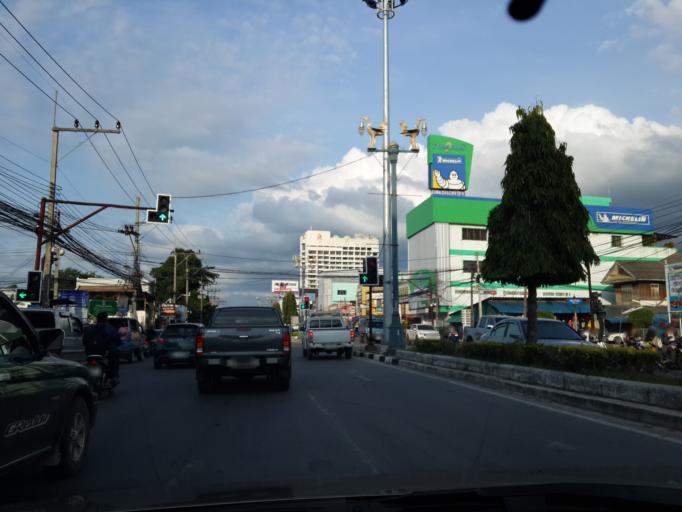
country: TH
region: Yala
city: Yala
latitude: 6.5542
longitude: 101.2842
